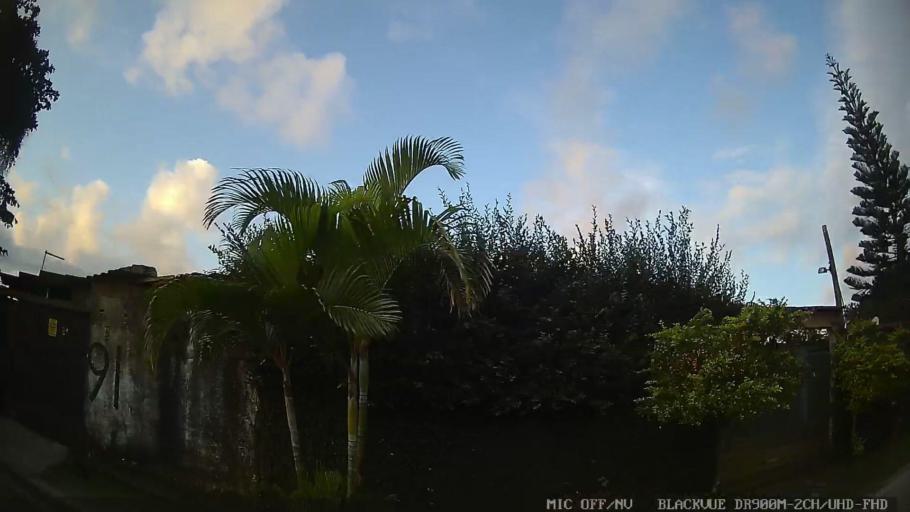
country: BR
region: Sao Paulo
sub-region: Itanhaem
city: Itanhaem
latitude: -24.1857
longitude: -46.8287
